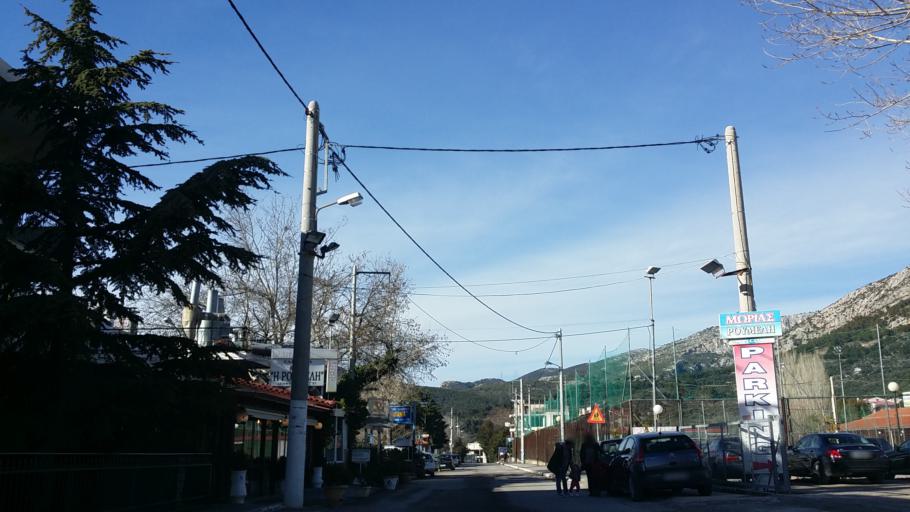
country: GR
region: Attica
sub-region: Nomarchia Dytikis Attikis
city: Fyli
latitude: 38.1063
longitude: 23.6681
